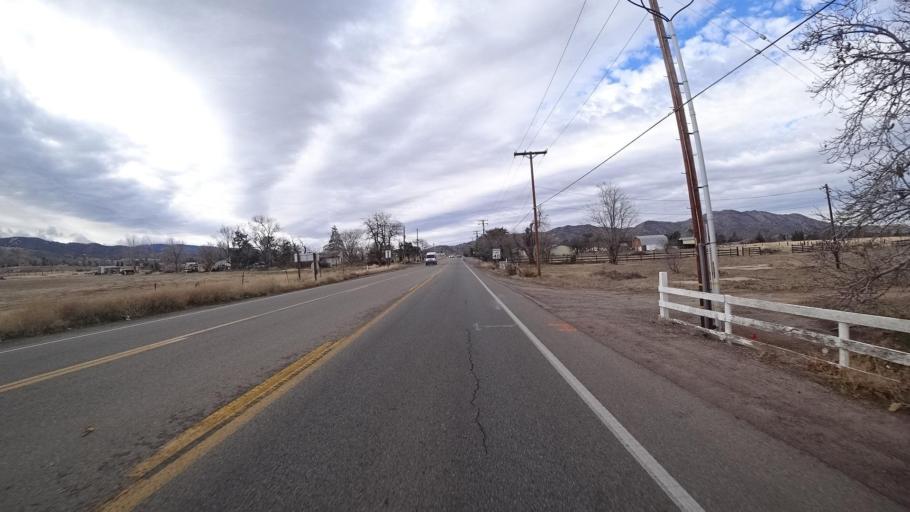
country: US
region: California
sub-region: Kern County
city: Tehachapi
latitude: 35.1243
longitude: -118.4704
